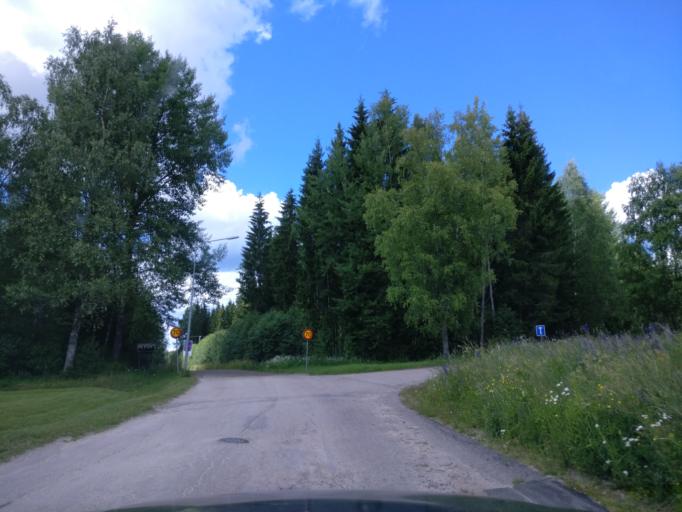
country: SE
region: Vaermland
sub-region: Hagfors Kommun
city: Hagfors
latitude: 60.0284
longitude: 13.6736
